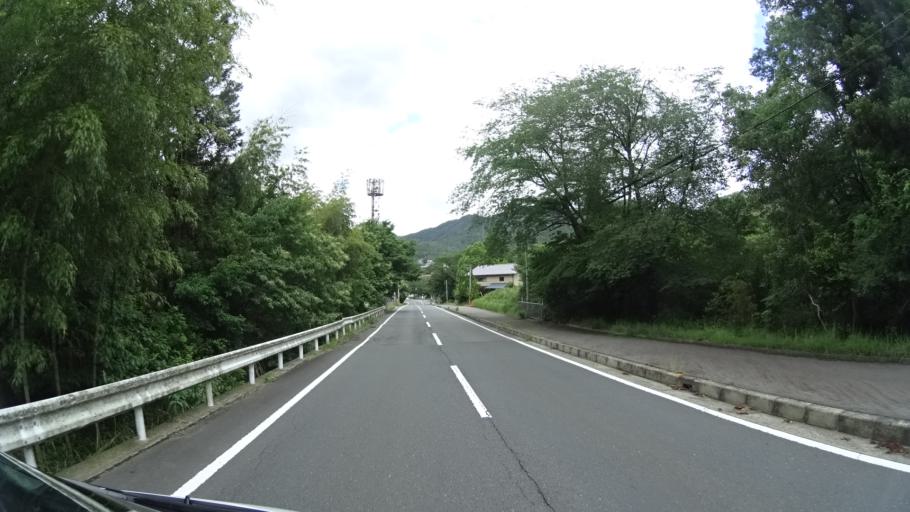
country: JP
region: Kyoto
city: Kameoka
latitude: 35.0134
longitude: 135.4337
